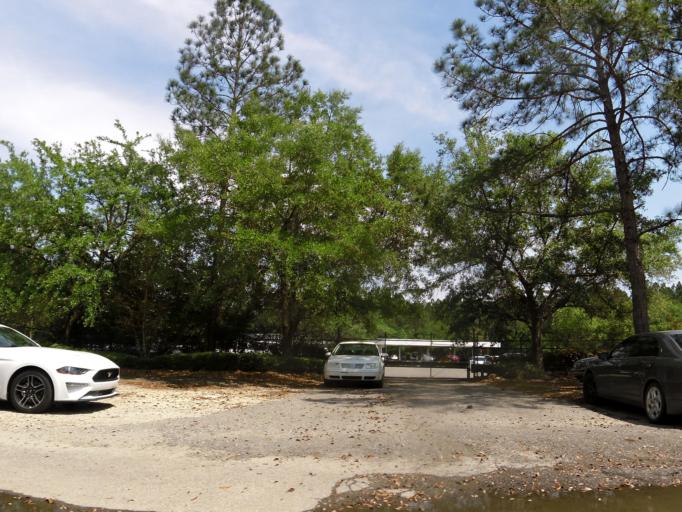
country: US
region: Florida
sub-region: Nassau County
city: Nassau Village-Ratliff
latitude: 30.4921
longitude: -81.6676
